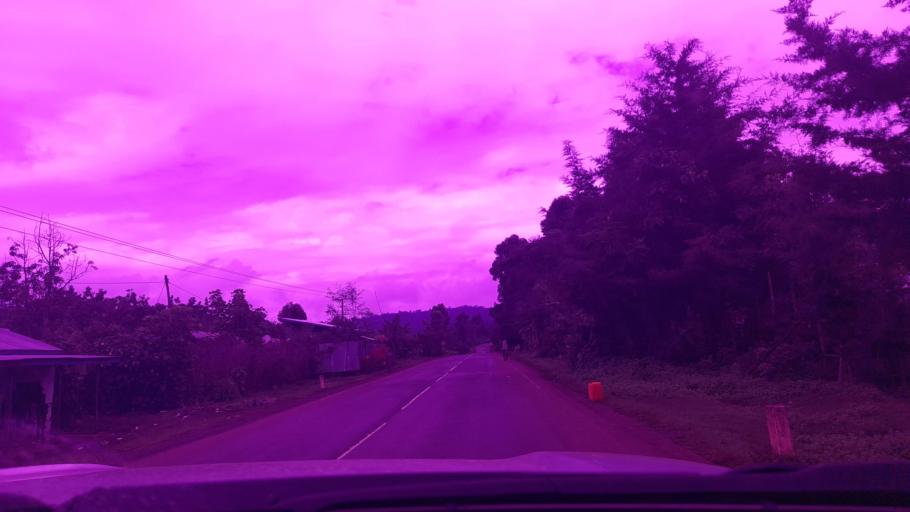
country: ET
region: Oromiya
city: Jima
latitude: 7.5548
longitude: 36.6139
